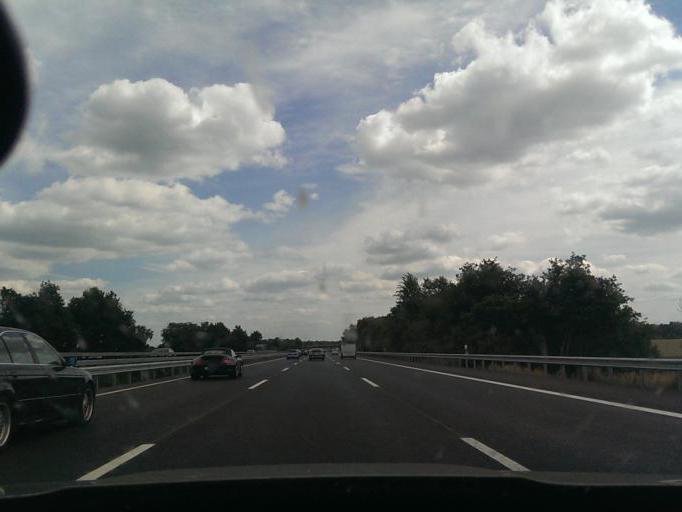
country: DE
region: Lower Saxony
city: Hademstorf
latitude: 52.7239
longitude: 9.6794
